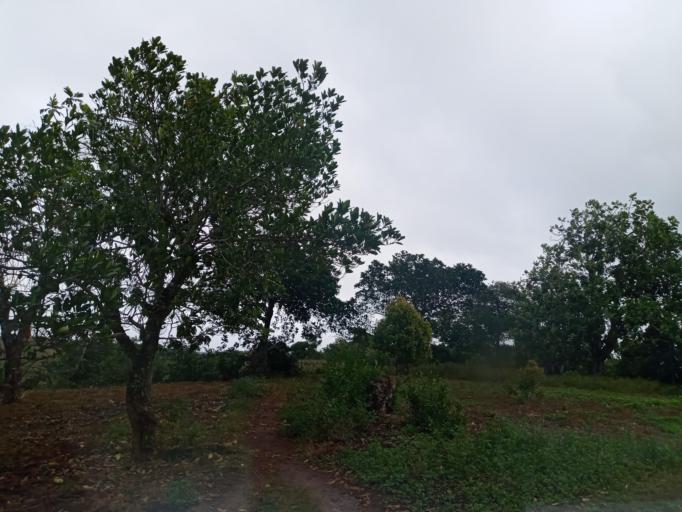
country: MG
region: Atsimo-Atsinanana
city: Vohipaho
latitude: -23.8288
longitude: 47.5425
